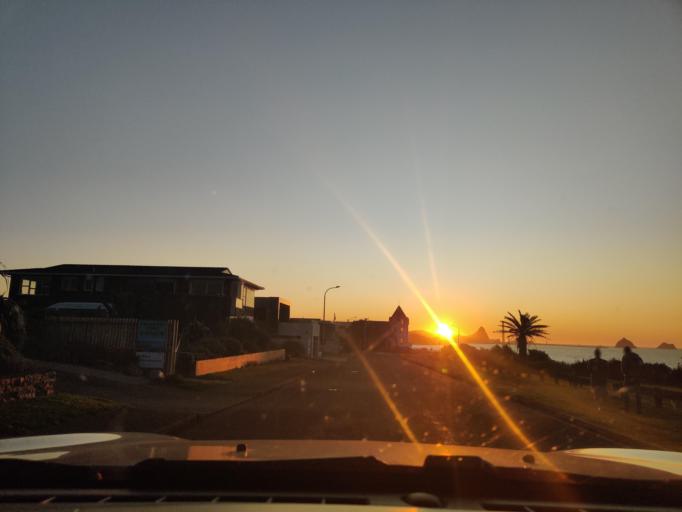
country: NZ
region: Taranaki
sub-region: New Plymouth District
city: New Plymouth
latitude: -39.0515
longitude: 174.0825
